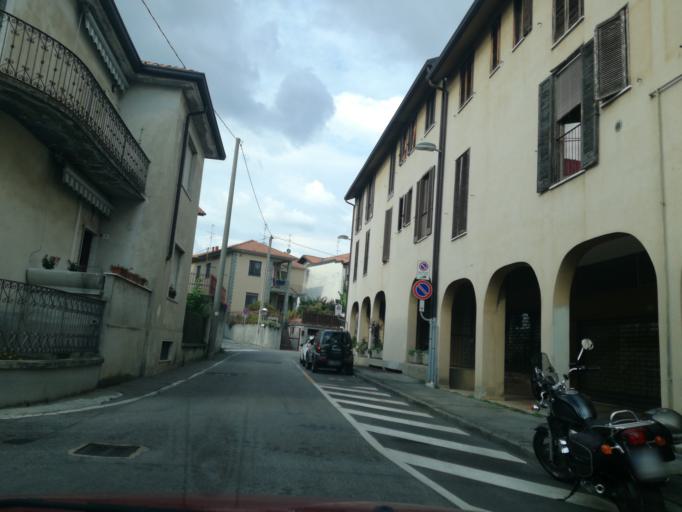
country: IT
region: Lombardy
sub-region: Provincia di Monza e Brianza
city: Villanova
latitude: 45.6274
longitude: 9.3861
